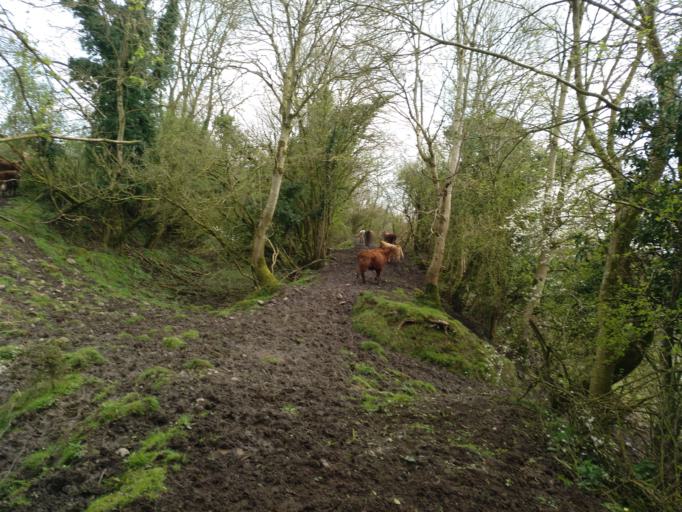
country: IE
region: Ulster
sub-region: County Monaghan
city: Clones
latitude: 54.2003
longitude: -7.1382
